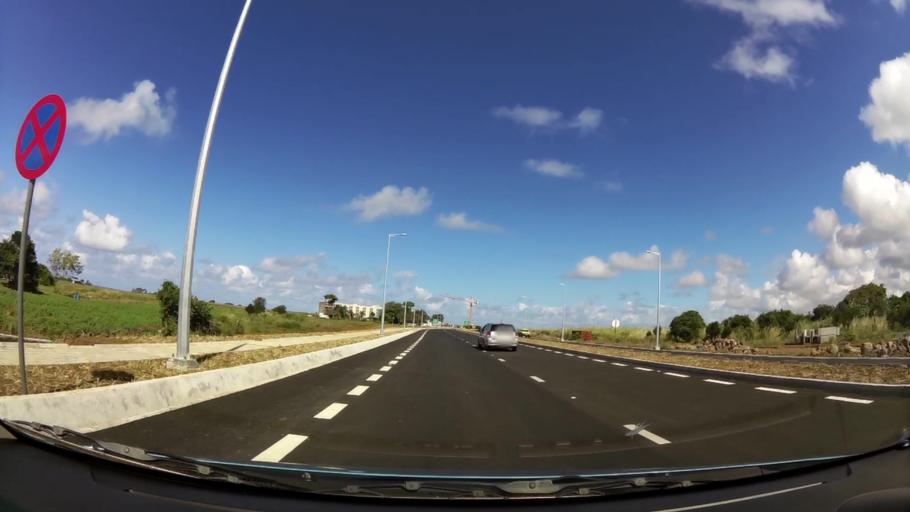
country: MU
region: Grand Port
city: Plaine Magnien
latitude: -20.4367
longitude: 57.6729
